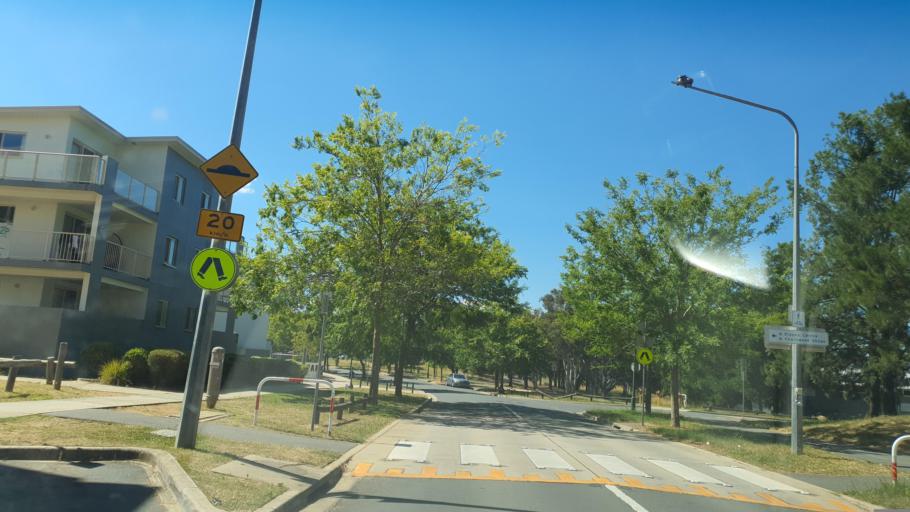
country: AU
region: Australian Capital Territory
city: Macquarie
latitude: -35.2352
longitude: 149.0655
